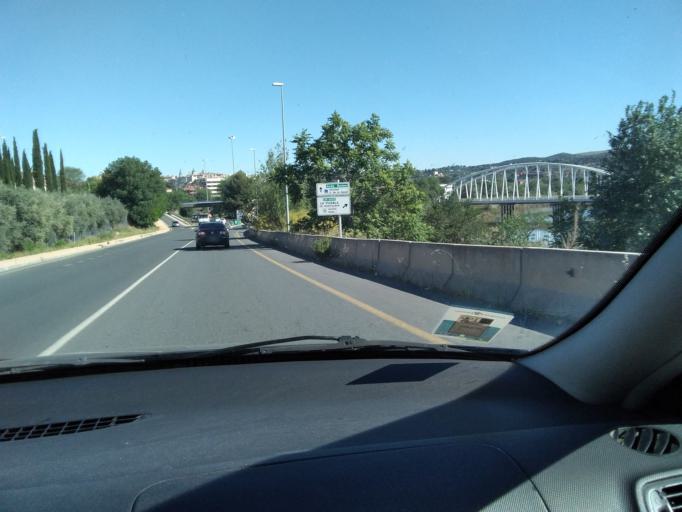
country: ES
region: Castille-La Mancha
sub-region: Province of Toledo
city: Toledo
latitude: 39.8768
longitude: -4.0443
